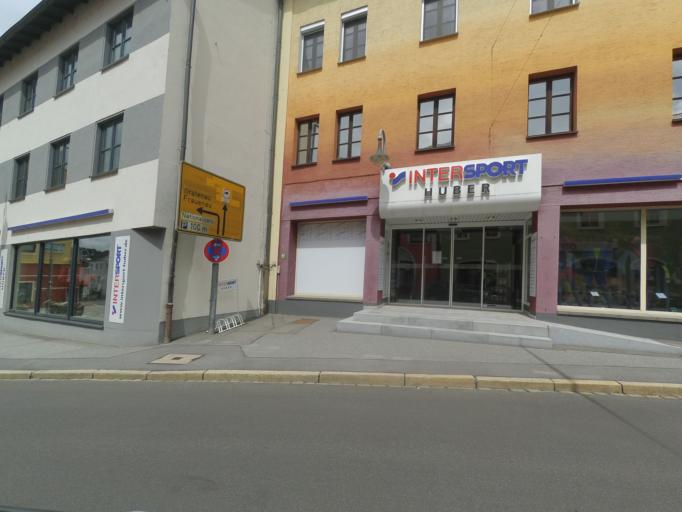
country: DE
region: Bavaria
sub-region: Lower Bavaria
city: Zwiesel
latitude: 49.0141
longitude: 13.2329
